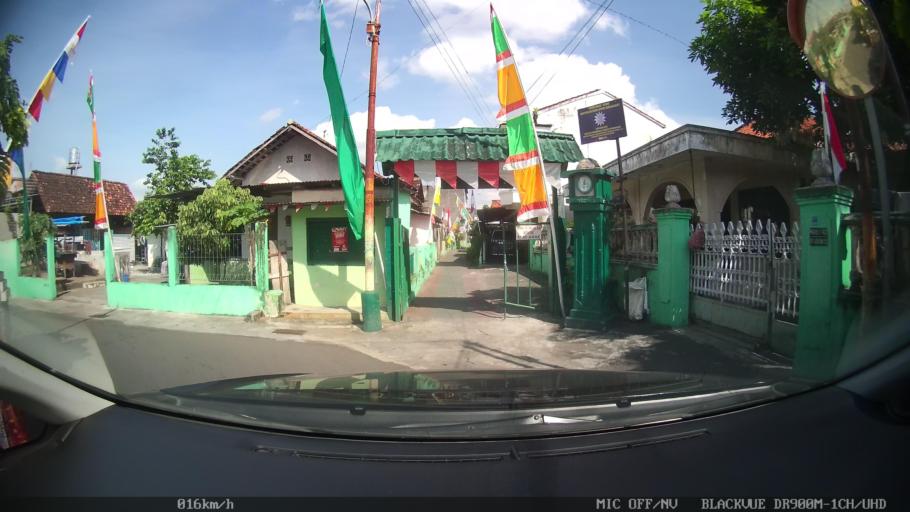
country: ID
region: Daerah Istimewa Yogyakarta
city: Yogyakarta
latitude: -7.8225
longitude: 110.3705
